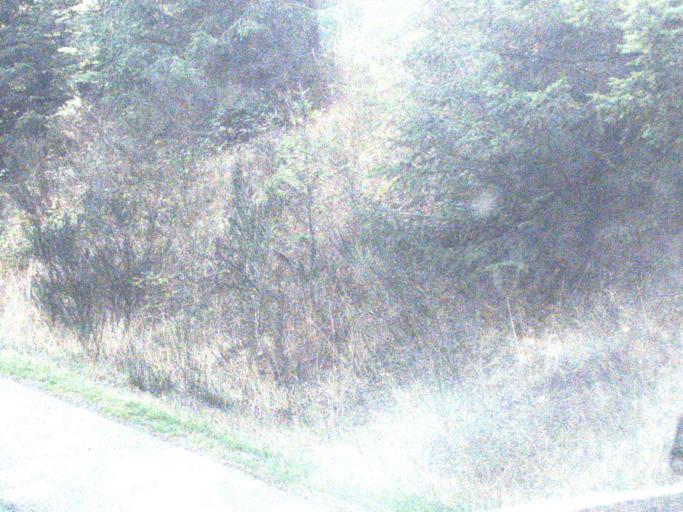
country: US
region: Washington
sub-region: Island County
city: Coupeville
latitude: 48.2204
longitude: -122.7339
